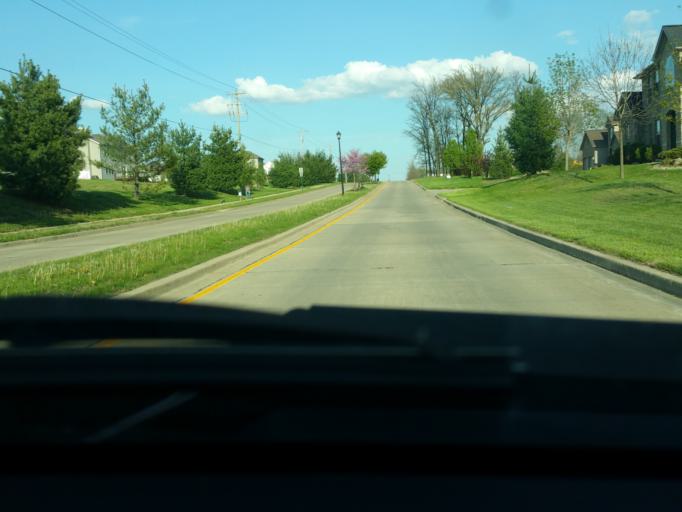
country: US
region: Illinois
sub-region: Madison County
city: Edwardsville
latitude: 38.7813
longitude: -89.9352
